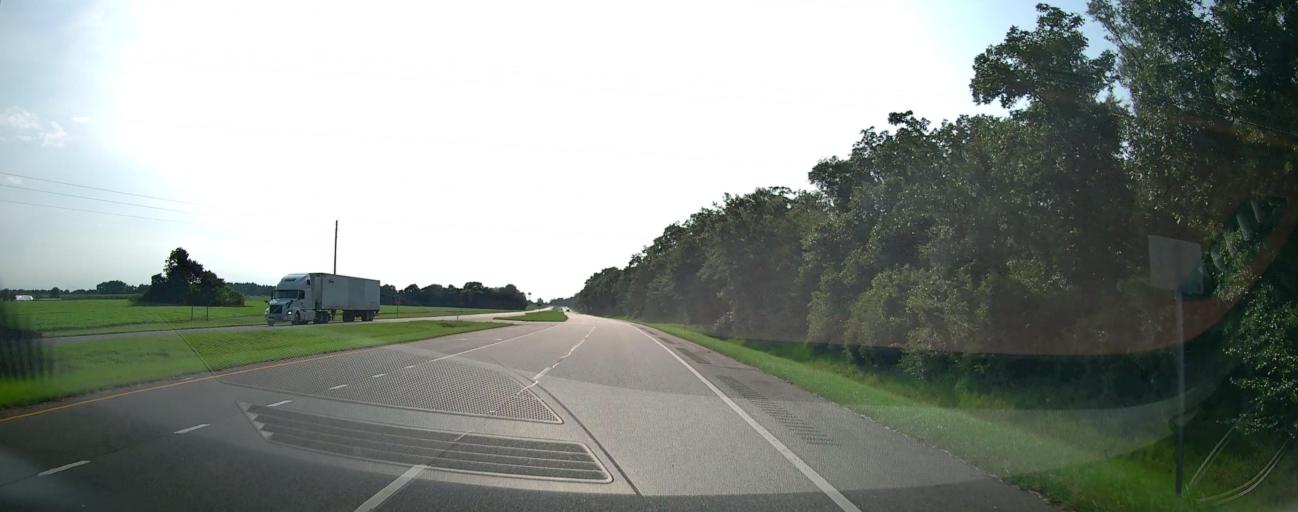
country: US
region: Georgia
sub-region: Taylor County
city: Reynolds
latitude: 32.5575
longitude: -84.0650
